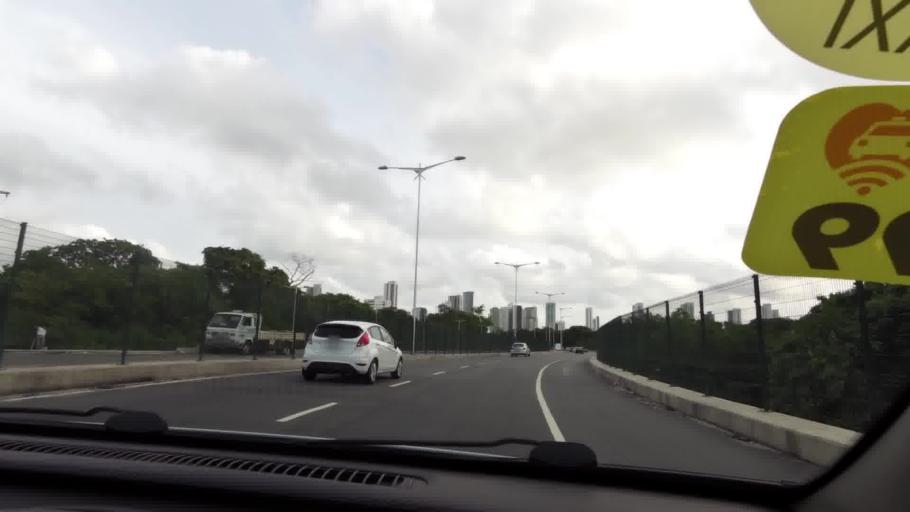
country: BR
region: Pernambuco
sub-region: Recife
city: Recife
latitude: -8.0973
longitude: -34.8910
